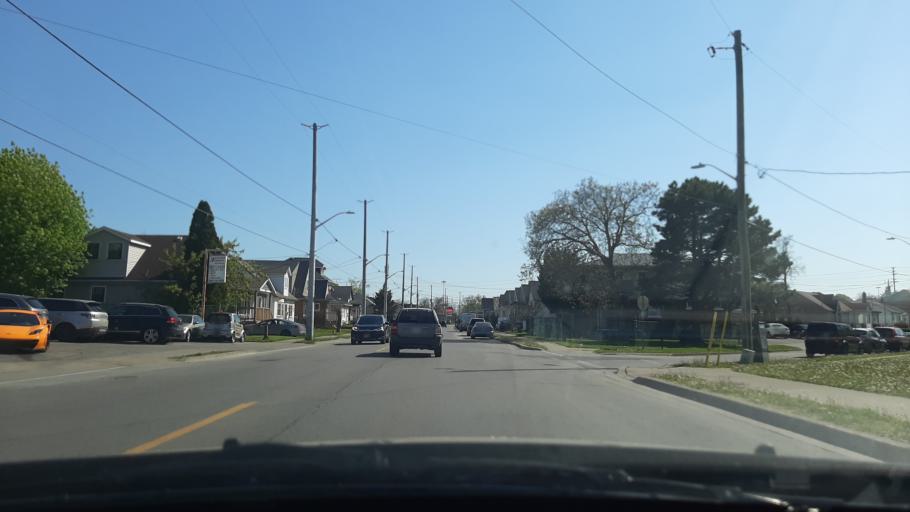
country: CA
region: Ontario
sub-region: Regional Municipality of Niagara
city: St. Catharines
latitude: 43.1772
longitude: -79.2285
